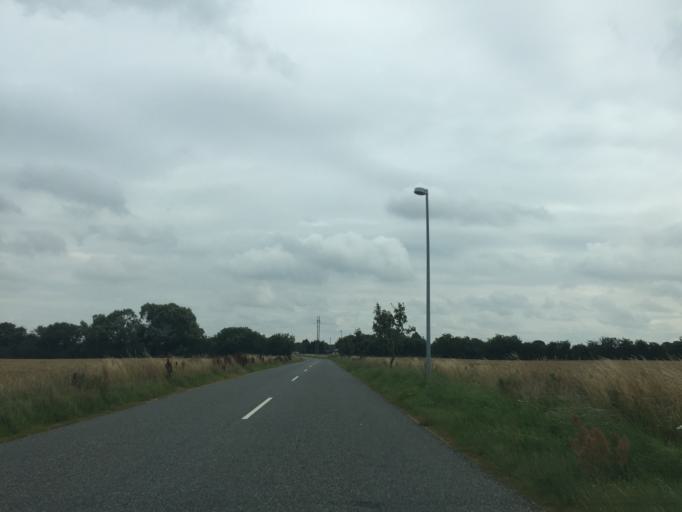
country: DK
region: Central Jutland
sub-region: Viborg Kommune
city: Bjerringbro
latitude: 56.2599
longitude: 9.7145
